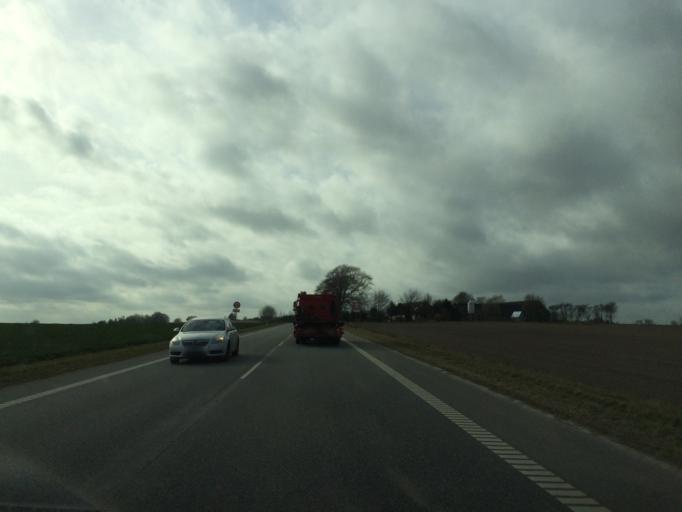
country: DK
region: Central Jutland
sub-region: Randers Kommune
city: Langa
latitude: 56.4789
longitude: 9.9021
